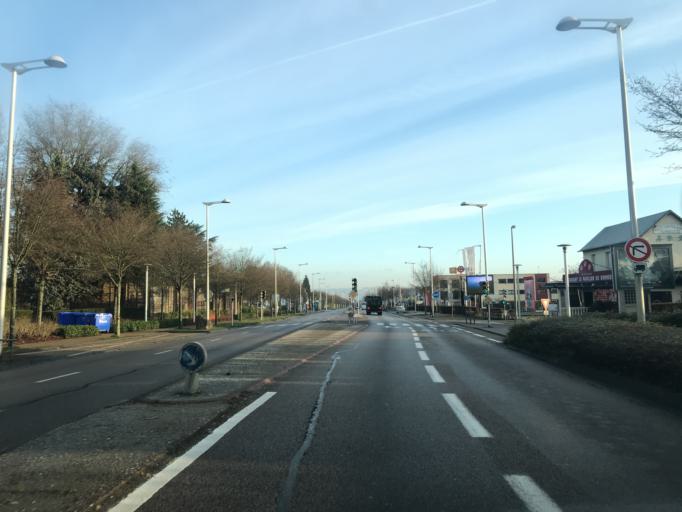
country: FR
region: Haute-Normandie
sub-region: Departement de la Seine-Maritime
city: Le Petit-Quevilly
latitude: 49.4003
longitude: 1.0640
